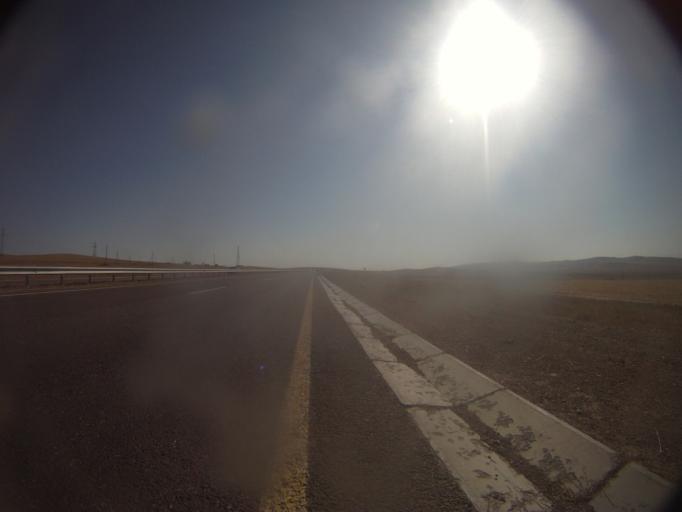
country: KZ
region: Ongtustik Qazaqstan
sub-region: Tulkibas Audany
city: Zhabagly
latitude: 42.7220
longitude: 70.8798
